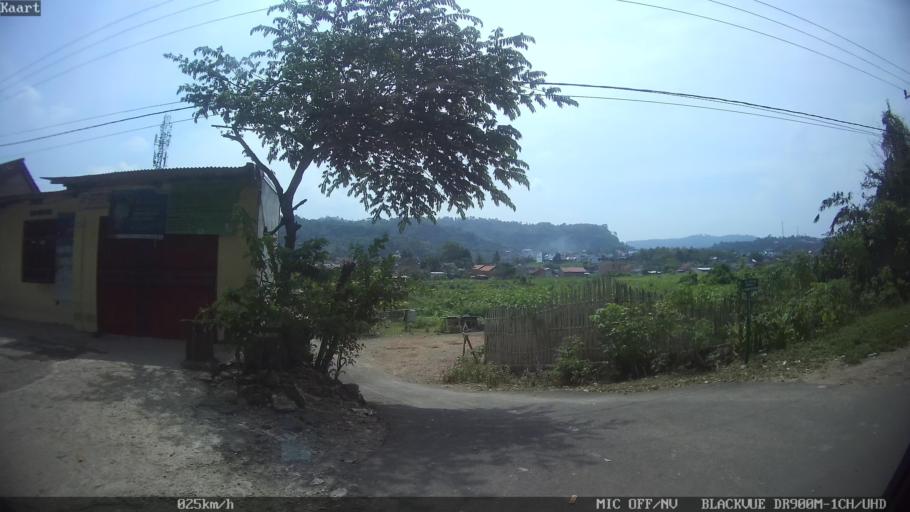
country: ID
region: Lampung
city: Bandarlampung
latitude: -5.4541
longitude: 105.2478
